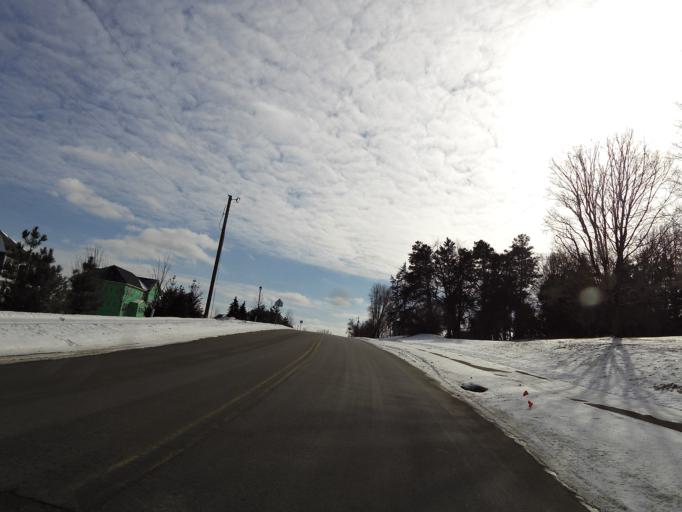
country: US
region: Minnesota
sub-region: Hennepin County
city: Eden Prairie
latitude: 44.8258
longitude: -93.4853
